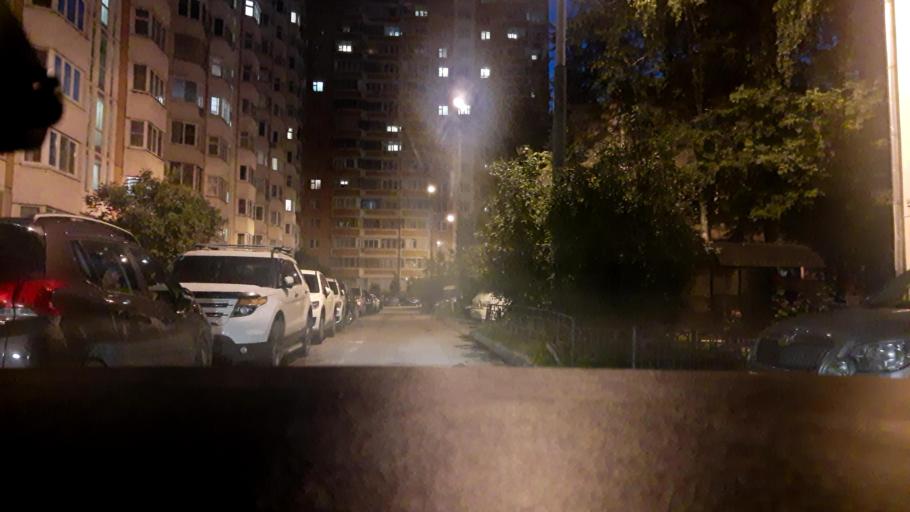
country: RU
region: Moskovskaya
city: Odintsovo
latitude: 55.6725
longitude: 37.2681
